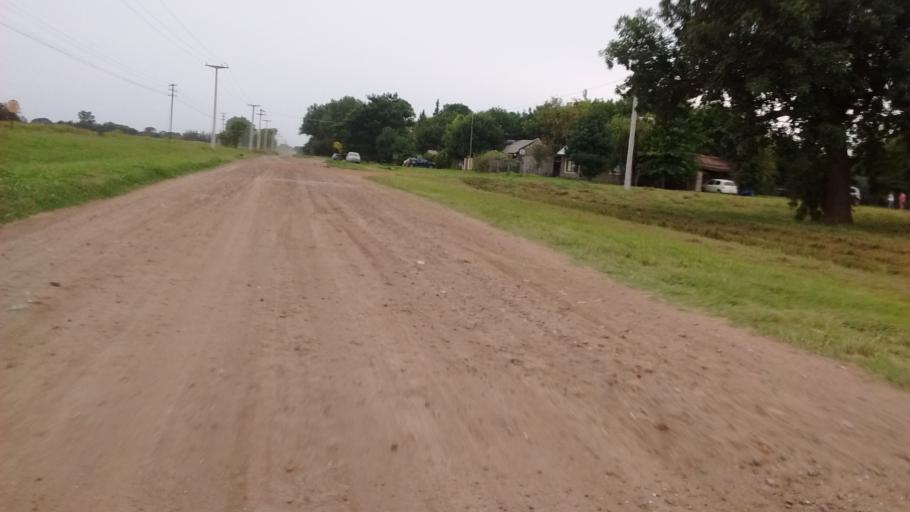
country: AR
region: Santa Fe
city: Funes
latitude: -32.9132
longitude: -60.8335
